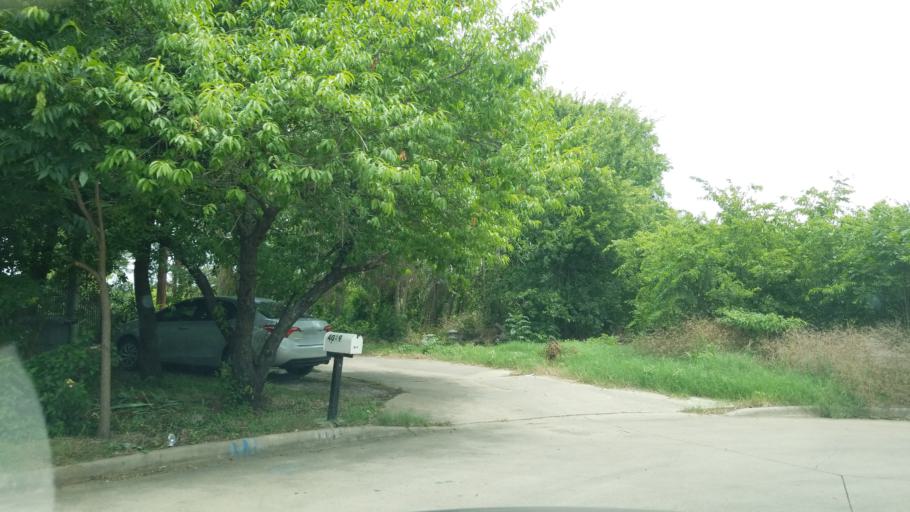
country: US
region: Texas
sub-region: Dallas County
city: Irving
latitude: 32.7908
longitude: -96.9057
